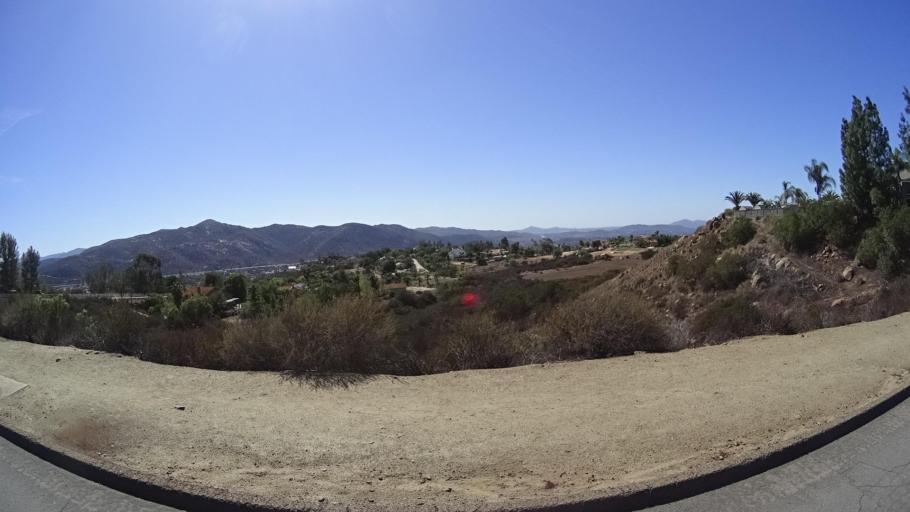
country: US
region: California
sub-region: San Diego County
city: Harbison Canyon
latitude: 32.8741
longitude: -116.8336
